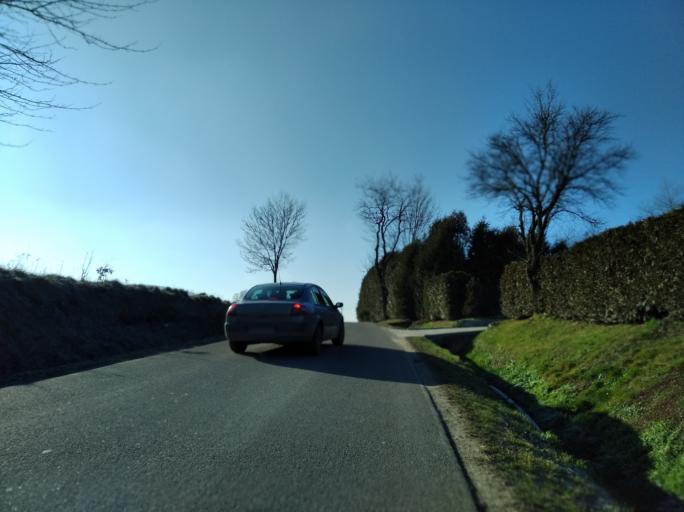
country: PL
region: Subcarpathian Voivodeship
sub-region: Powiat strzyzowski
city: Strzyzow
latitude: 49.8546
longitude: 21.7803
